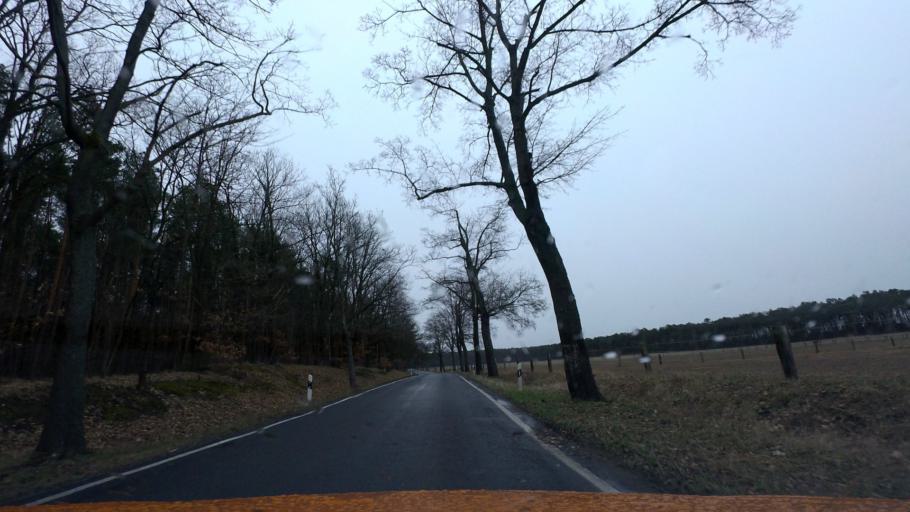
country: DE
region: Brandenburg
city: Brieselang
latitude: 52.6472
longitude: 13.0079
